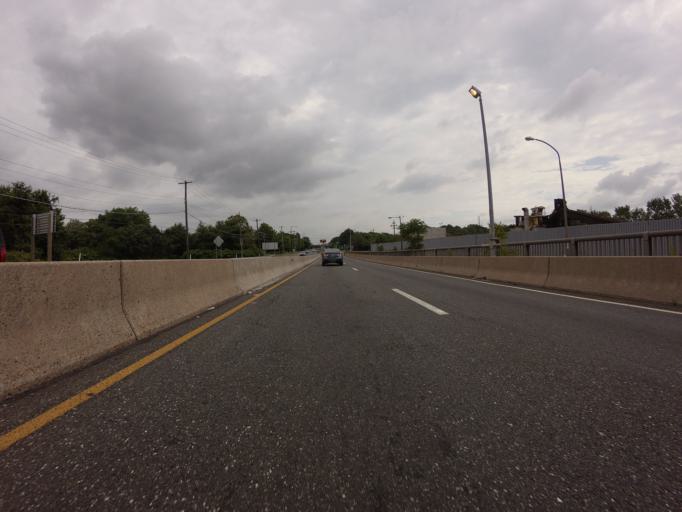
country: US
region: New Jersey
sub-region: Gloucester County
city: National Park
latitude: 39.9039
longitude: -75.1979
